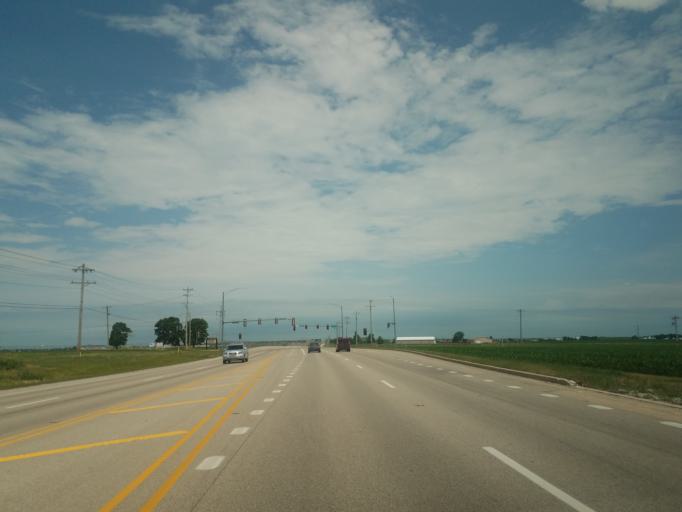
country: US
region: Illinois
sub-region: McLean County
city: Downs
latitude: 40.4716
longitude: -88.9021
